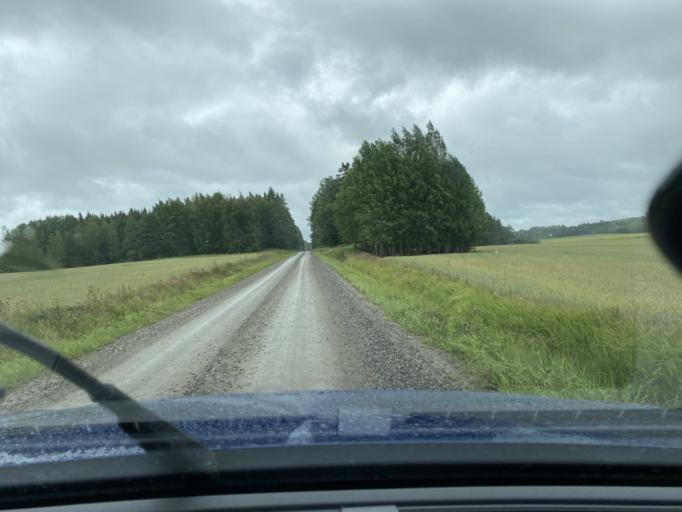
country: FI
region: Pirkanmaa
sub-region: Lounais-Pirkanmaa
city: Punkalaidun
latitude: 61.1499
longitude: 23.2307
